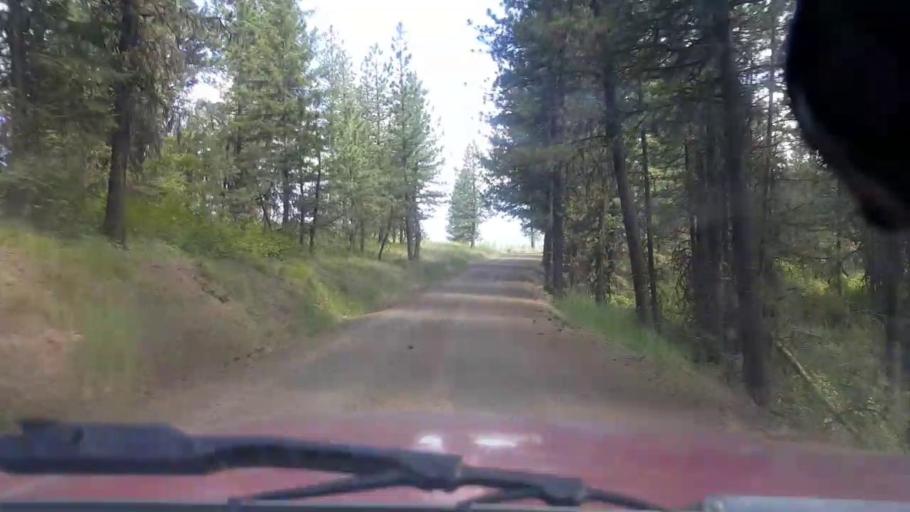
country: US
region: Washington
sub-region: Asotin County
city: Asotin
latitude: 46.0320
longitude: -117.4059
